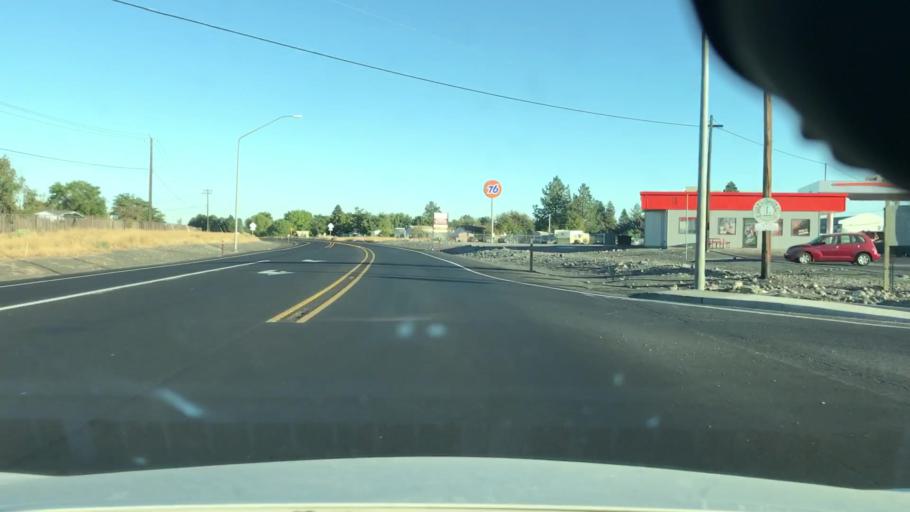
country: US
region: Washington
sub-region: Grant County
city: Cascade Valley
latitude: 47.1617
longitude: -119.3236
